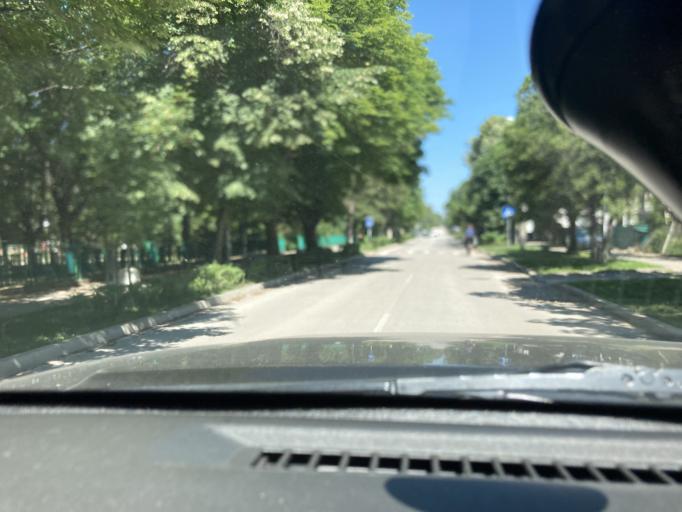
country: BG
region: Sofiya
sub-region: Obshtina Slivnitsa
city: Slivnitsa
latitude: 42.8539
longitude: 23.0363
